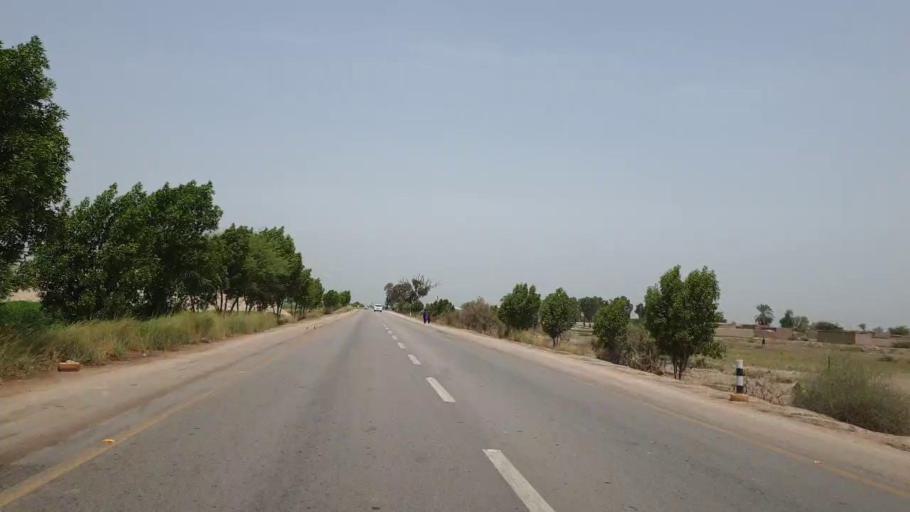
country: PK
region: Sindh
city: Nawabshah
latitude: 26.2259
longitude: 68.4923
